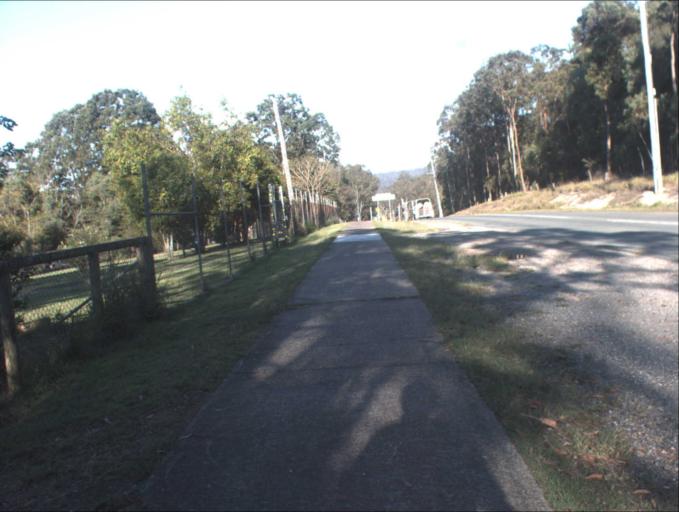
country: AU
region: Queensland
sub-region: Logan
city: Chambers Flat
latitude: -27.7666
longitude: 153.1146
